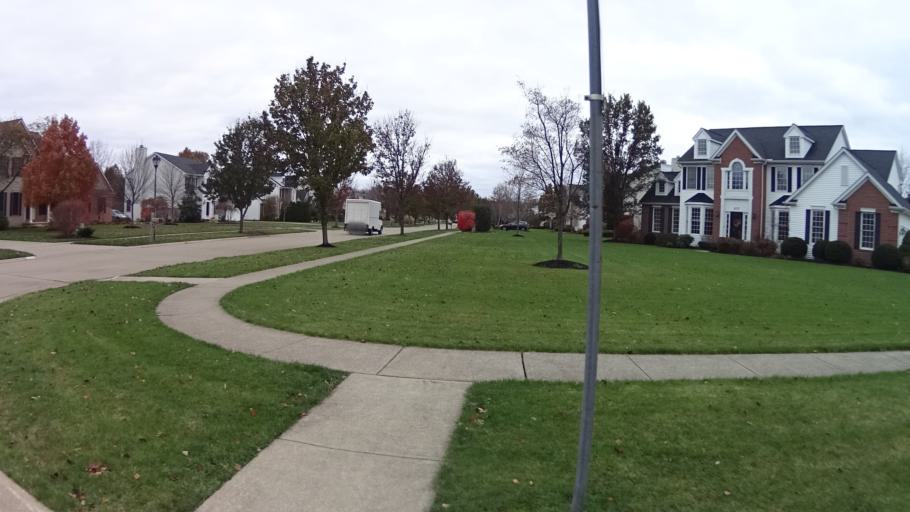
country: US
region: Ohio
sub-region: Lorain County
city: Avon Center
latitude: 41.4888
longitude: -81.9787
